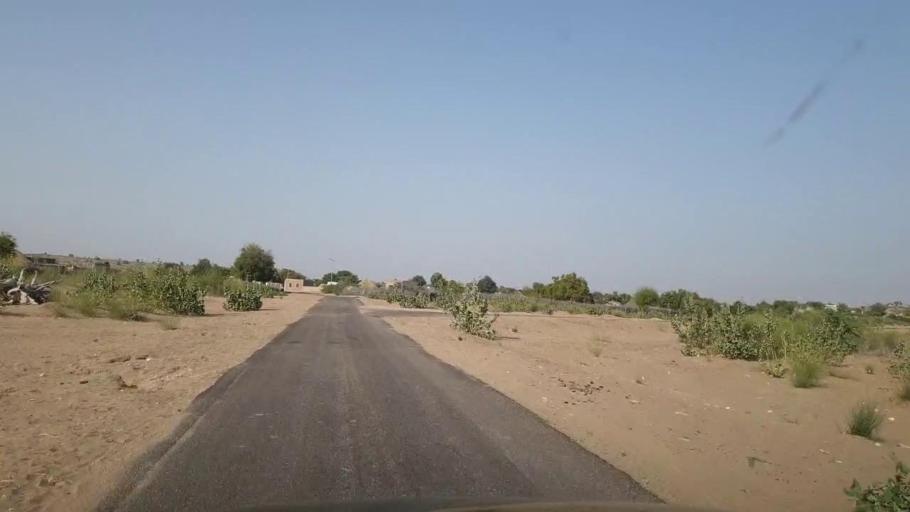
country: PK
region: Sindh
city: Islamkot
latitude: 25.1582
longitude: 70.5229
